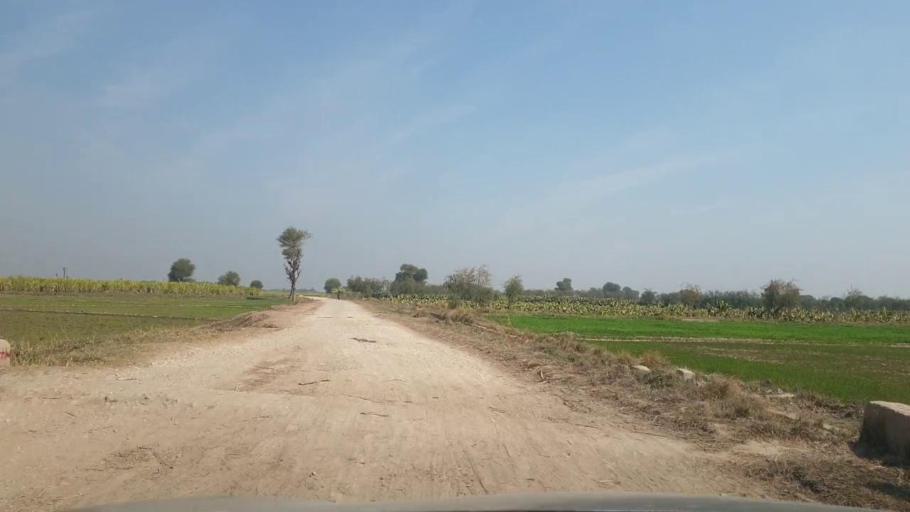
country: PK
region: Sindh
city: Tando Adam
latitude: 25.6357
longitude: 68.7199
